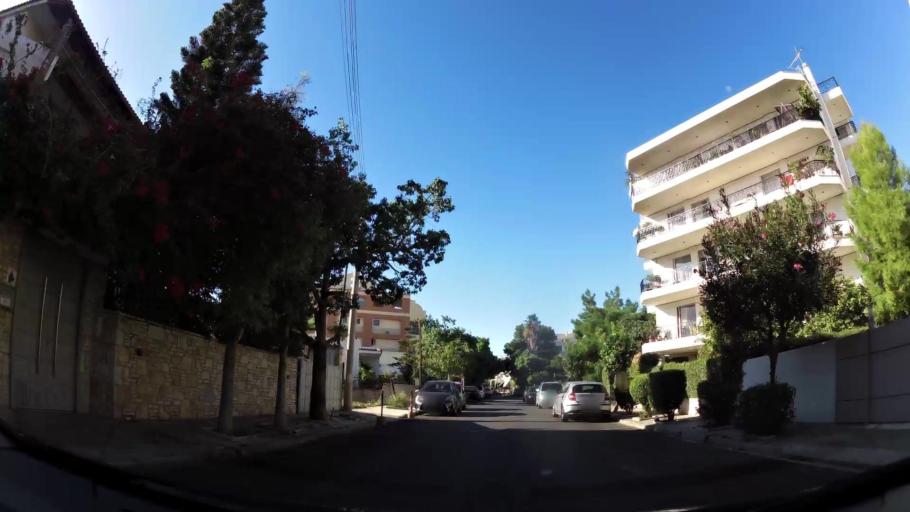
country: GR
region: Attica
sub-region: Nomarchia Anatolikis Attikis
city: Voula
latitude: 37.8395
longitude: 23.7688
